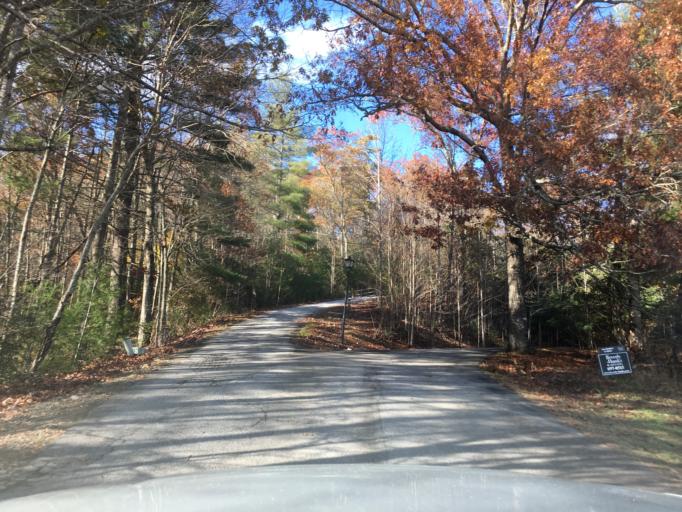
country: US
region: North Carolina
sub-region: Henderson County
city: Etowah
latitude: 35.3334
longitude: -82.6163
